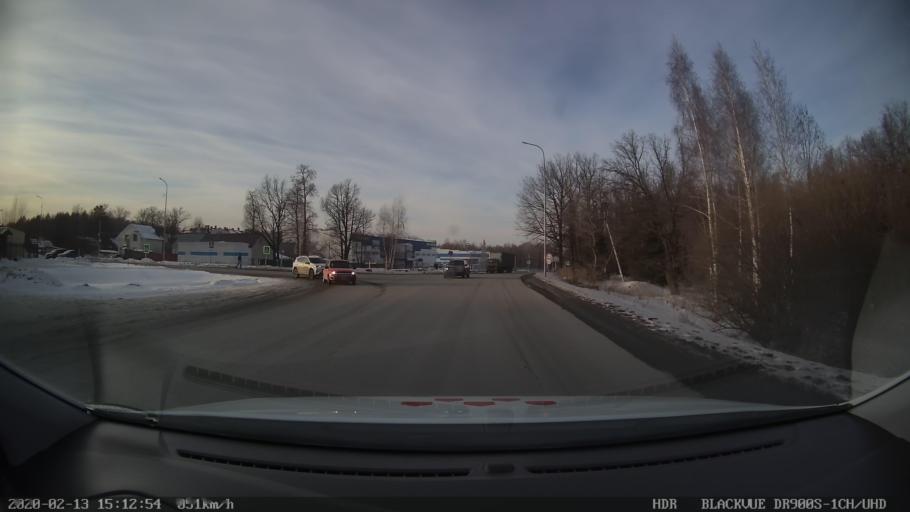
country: RU
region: Tatarstan
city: Vysokaya Gora
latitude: 55.9217
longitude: 49.3070
